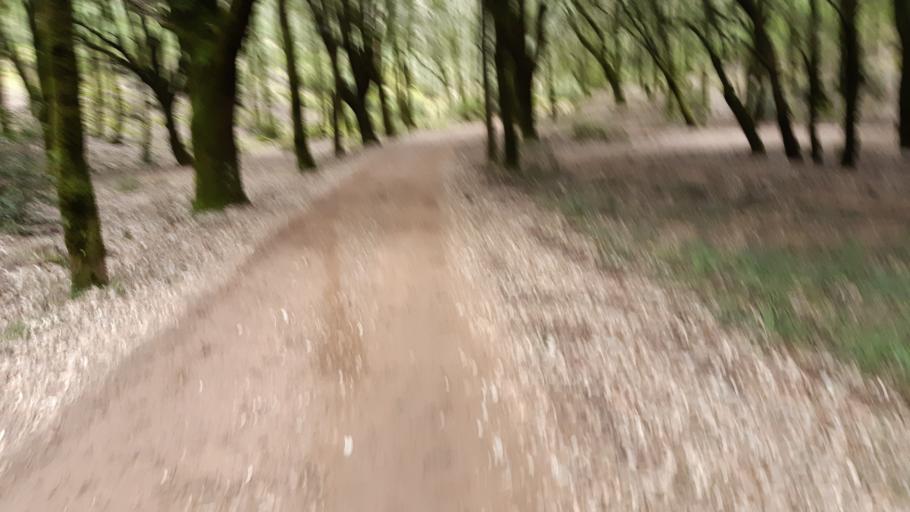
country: IT
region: Sardinia
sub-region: Provincia di Carbonia-Iglesias
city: Iglesias
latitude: 39.3862
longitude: 8.5712
